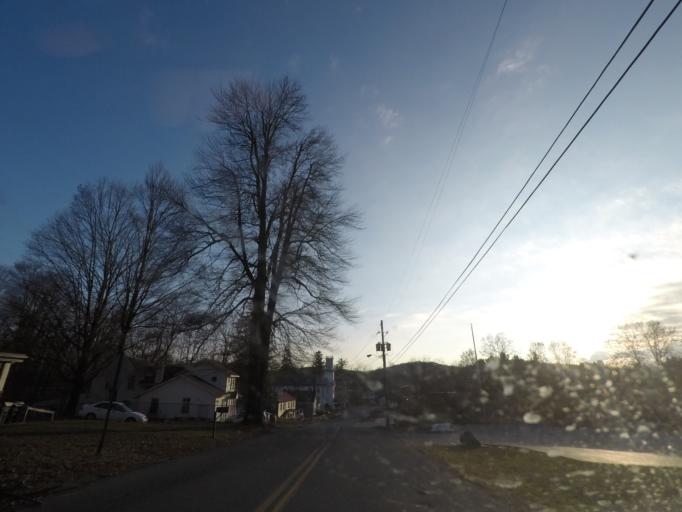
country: US
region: New York
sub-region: Rensselaer County
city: Wynantskill
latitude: 42.6946
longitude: -73.6332
